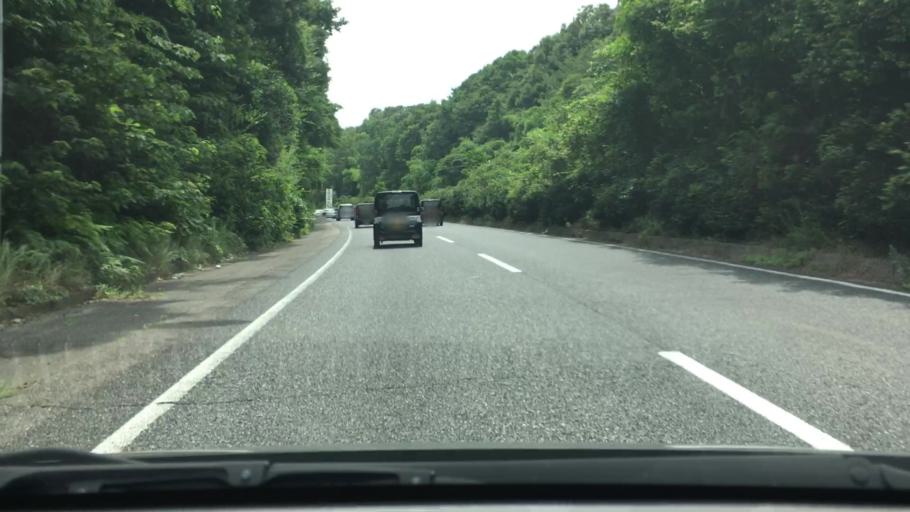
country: JP
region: Hiroshima
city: Hatsukaichi
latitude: 34.3716
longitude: 132.3362
